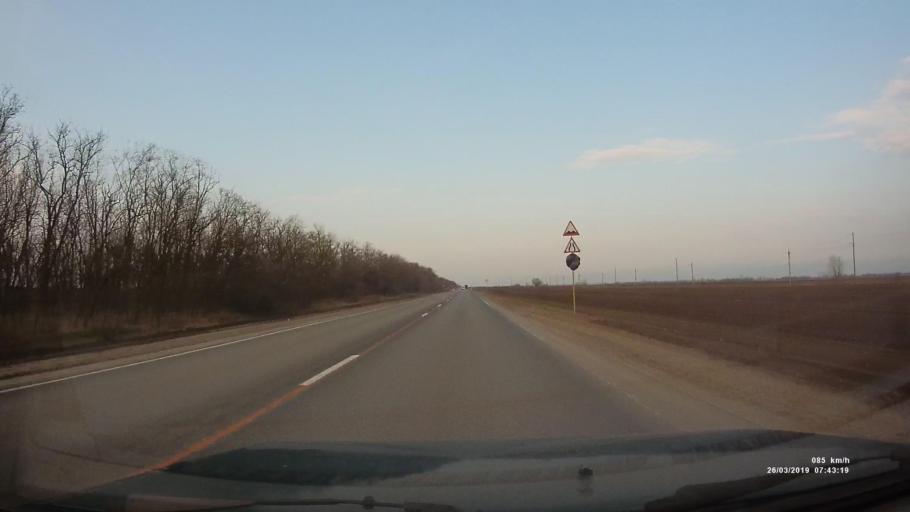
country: RU
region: Rostov
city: Novobessergenovka
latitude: 47.1830
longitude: 38.5973
